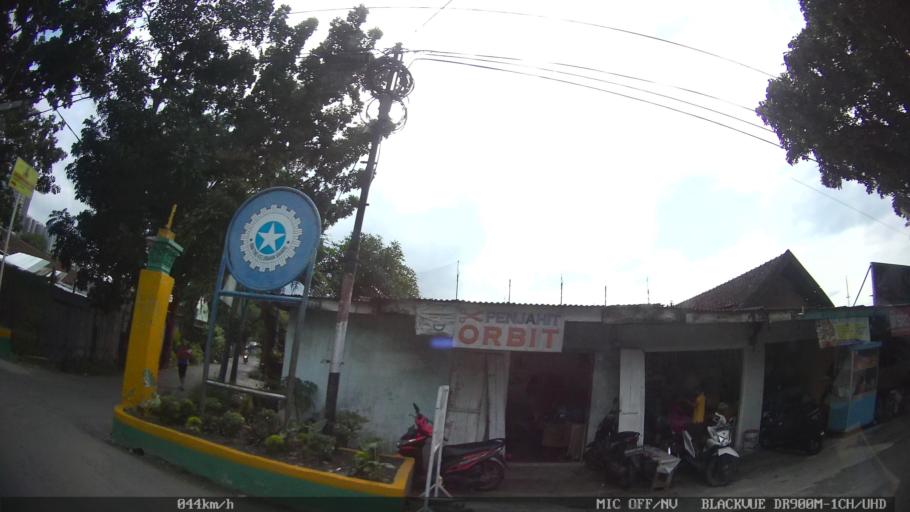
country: ID
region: North Sumatra
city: Medan
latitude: 3.6000
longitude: 98.6772
